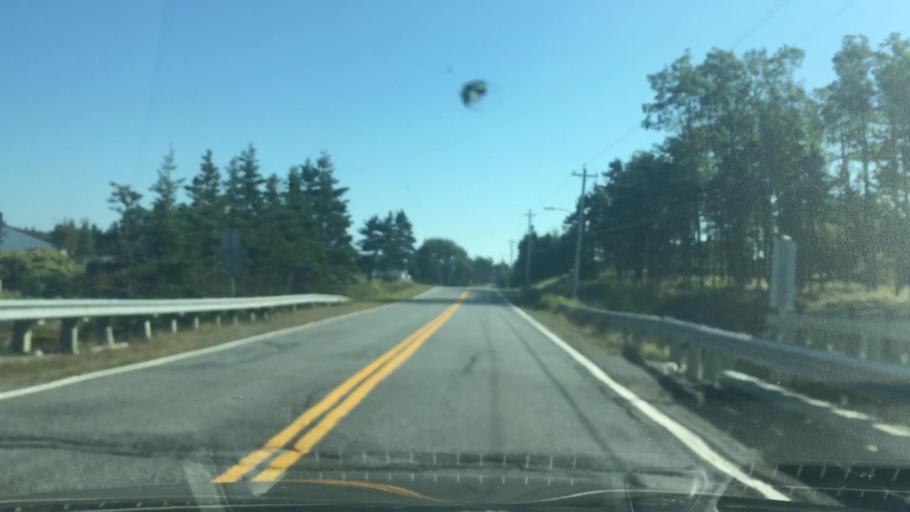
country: CA
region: Nova Scotia
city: Cole Harbour
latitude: 44.7778
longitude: -63.0122
